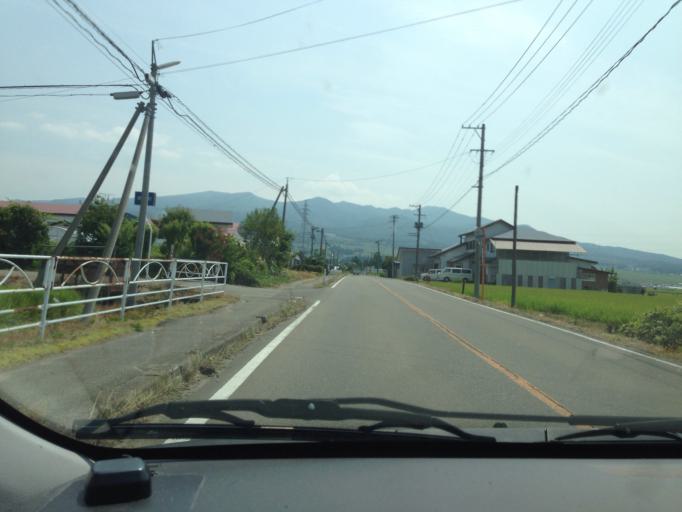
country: JP
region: Fukushima
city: Kitakata
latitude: 37.6461
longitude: 139.9033
